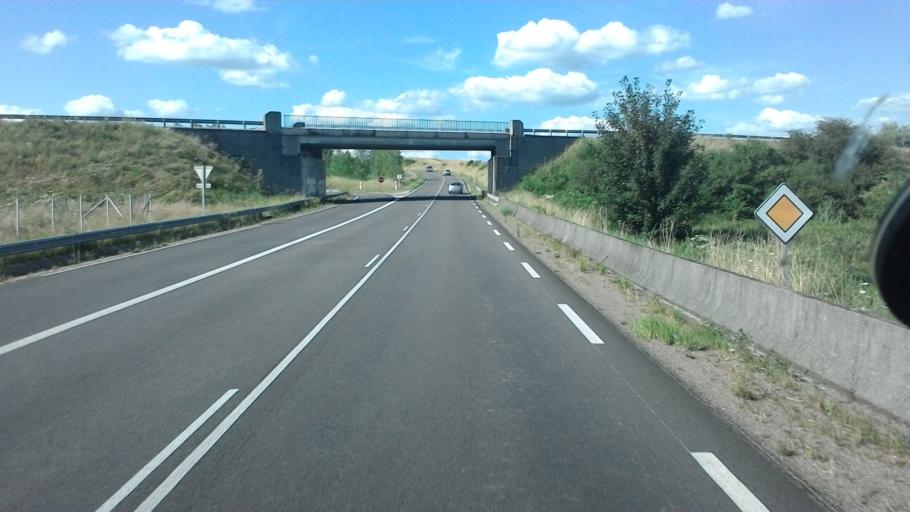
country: FR
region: Franche-Comte
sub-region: Departement de la Haute-Saone
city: Rioz
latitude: 47.4811
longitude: 5.9347
